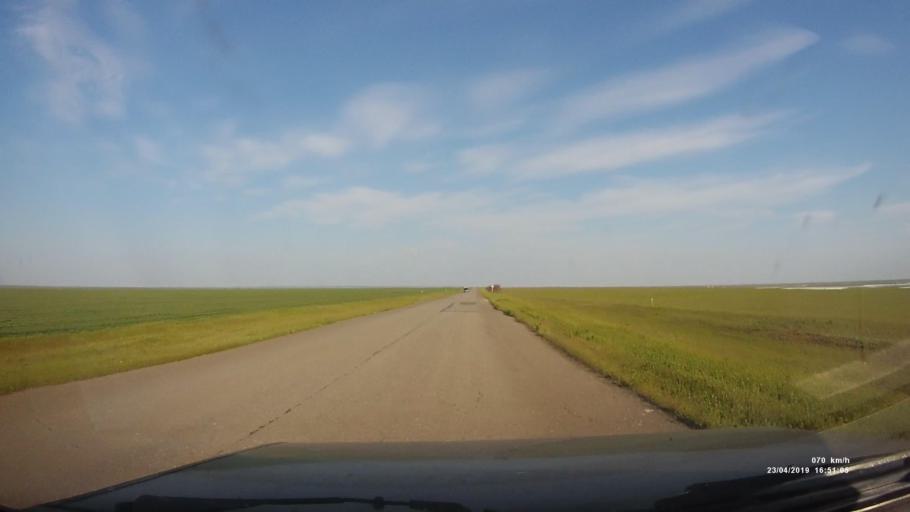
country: RU
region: Kalmykiya
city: Priyutnoye
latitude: 46.3244
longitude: 43.3010
